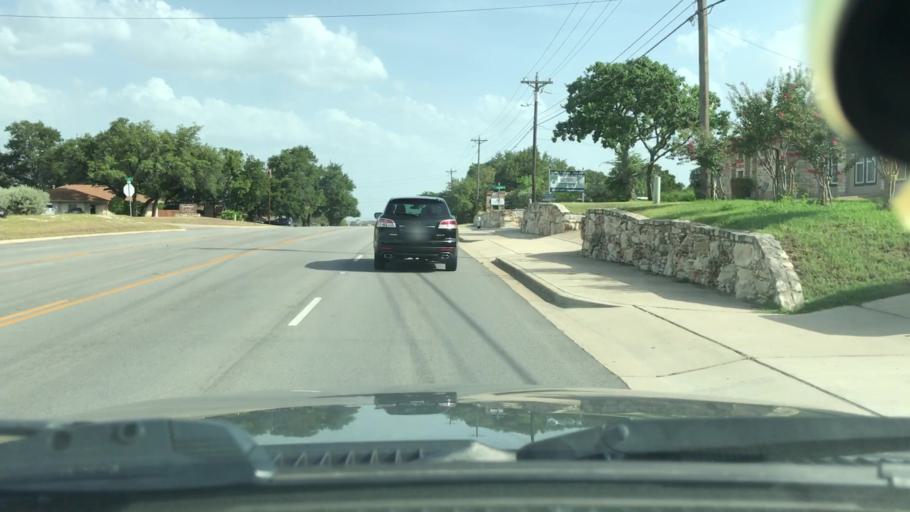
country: US
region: Texas
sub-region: Williamson County
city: Leander
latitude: 30.5444
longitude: -97.8511
